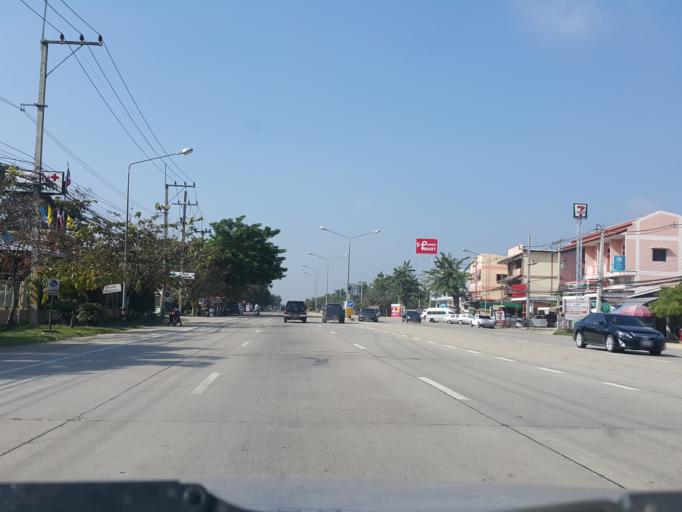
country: TH
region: Chiang Mai
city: San Sai
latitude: 18.8694
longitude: 99.1286
